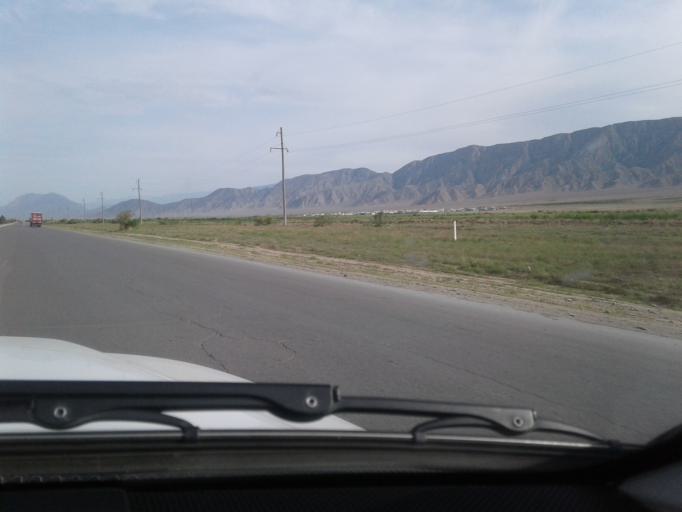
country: TM
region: Ahal
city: Arcabil
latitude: 38.2043
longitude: 57.8208
